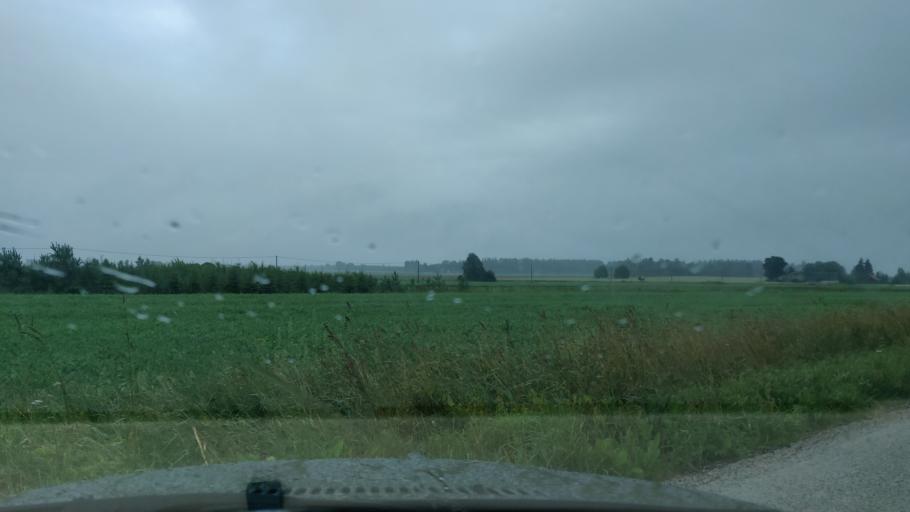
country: EE
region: Jaervamaa
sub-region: Jaerva-Jaani vald
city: Jarva-Jaani
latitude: 59.0927
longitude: 25.6992
